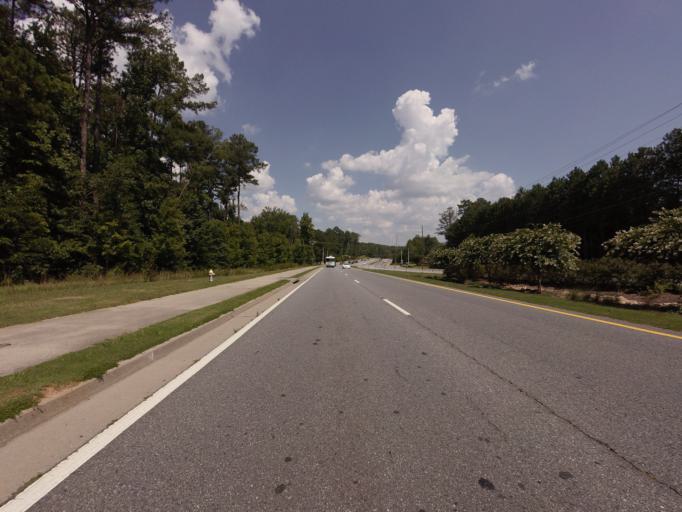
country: US
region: Georgia
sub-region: Fulton County
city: Johns Creek
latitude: 34.0308
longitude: -84.2083
